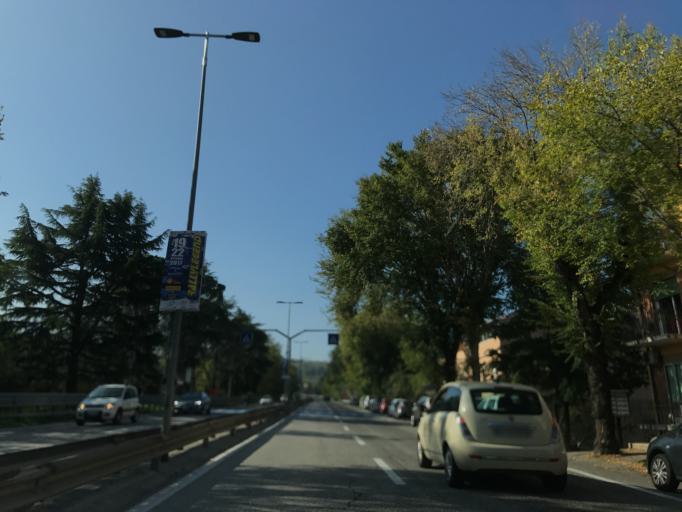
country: SM
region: Serravalle
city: Serravalle
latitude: 43.9671
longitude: 12.4749
